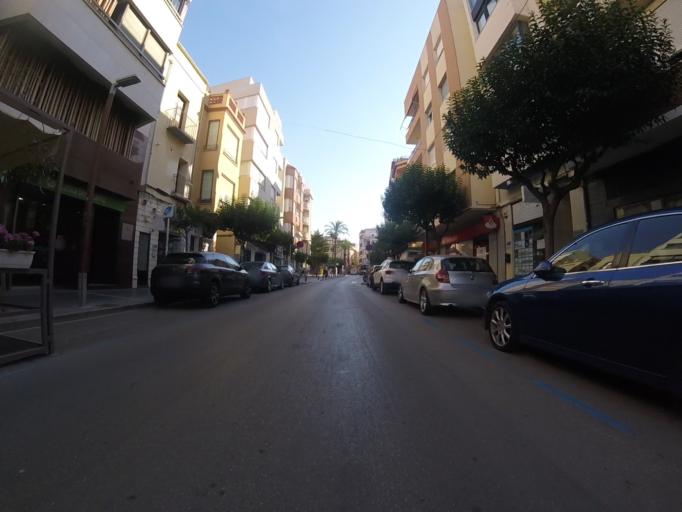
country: ES
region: Valencia
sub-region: Provincia de Castello
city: Benicarlo
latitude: 40.4181
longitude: 0.4249
